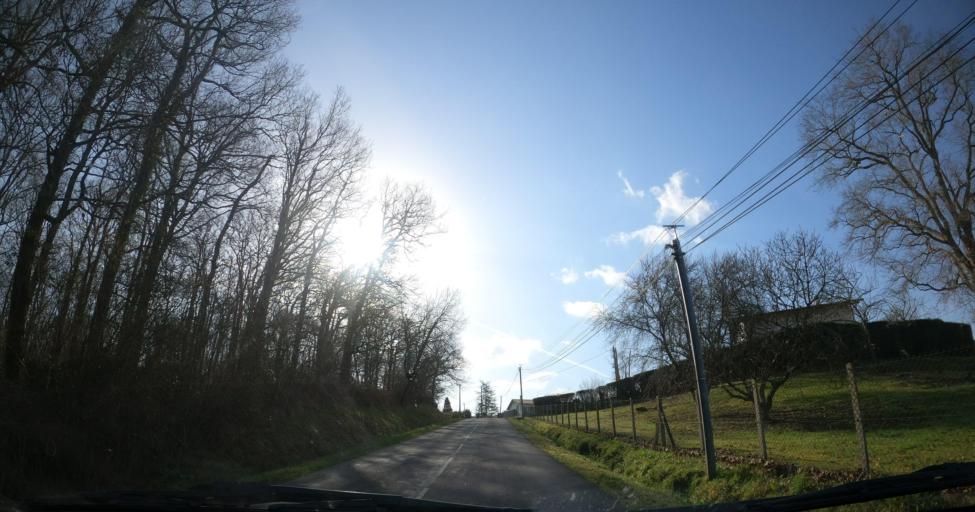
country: FR
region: Aquitaine
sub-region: Departement des Pyrenees-Atlantiques
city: Lahonce
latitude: 43.4522
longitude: -1.3708
